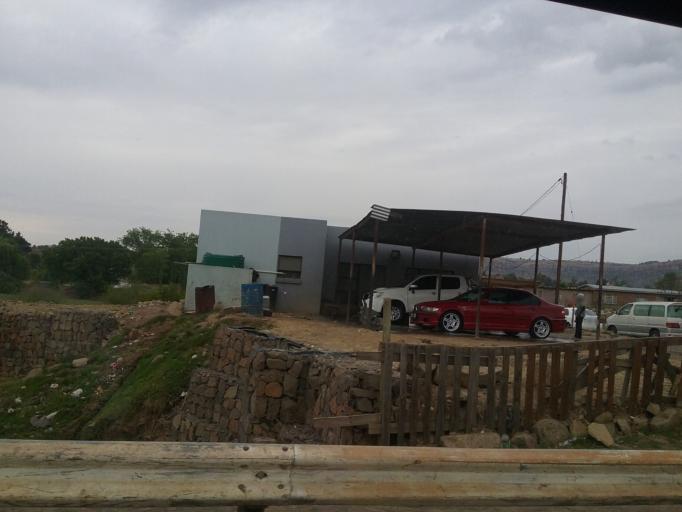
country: LS
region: Maseru
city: Maseru
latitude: -29.3176
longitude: 27.5100
